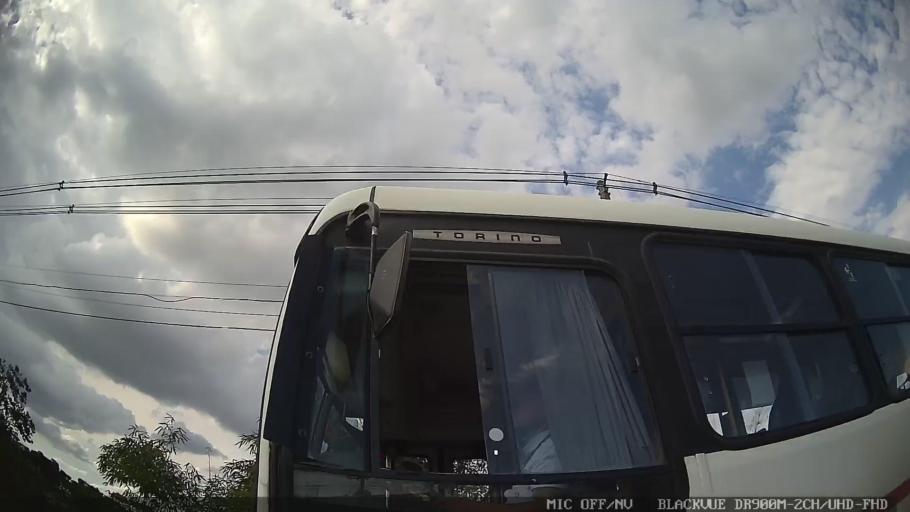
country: BR
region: Sao Paulo
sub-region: Itupeva
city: Itupeva
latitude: -23.1605
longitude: -47.0255
